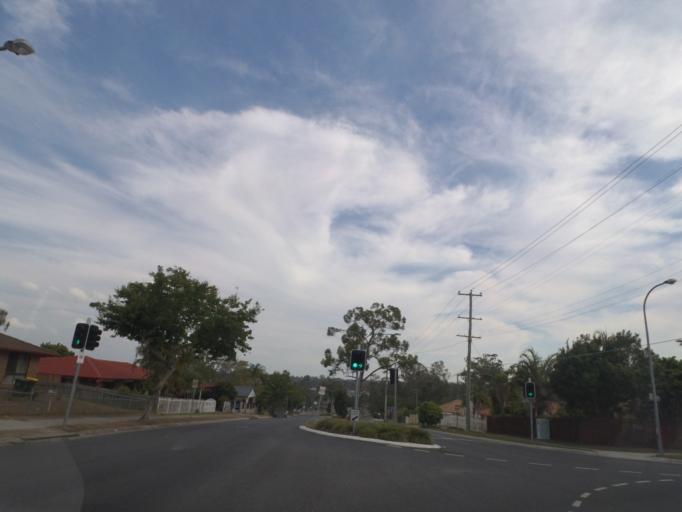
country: AU
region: Queensland
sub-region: Brisbane
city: Inala
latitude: -27.5888
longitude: 152.9765
